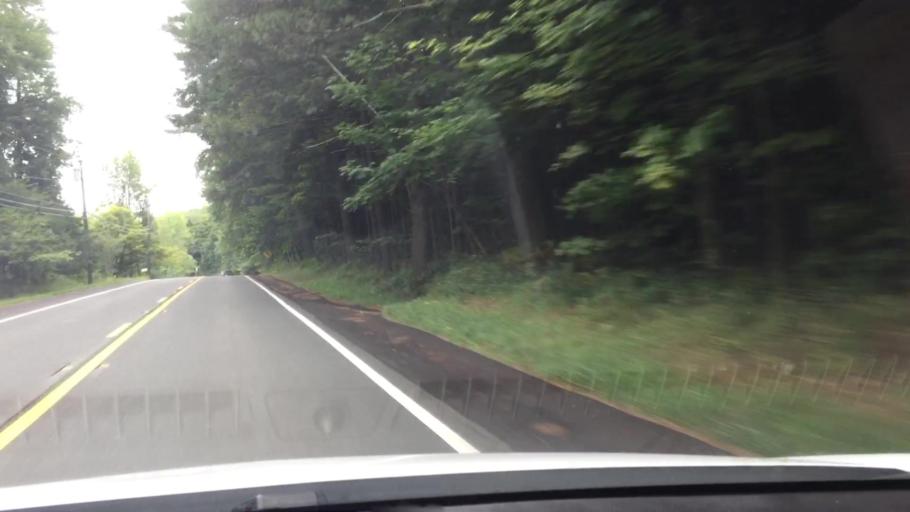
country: US
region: Massachusetts
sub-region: Berkshire County
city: Becket
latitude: 42.3589
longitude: -73.1030
